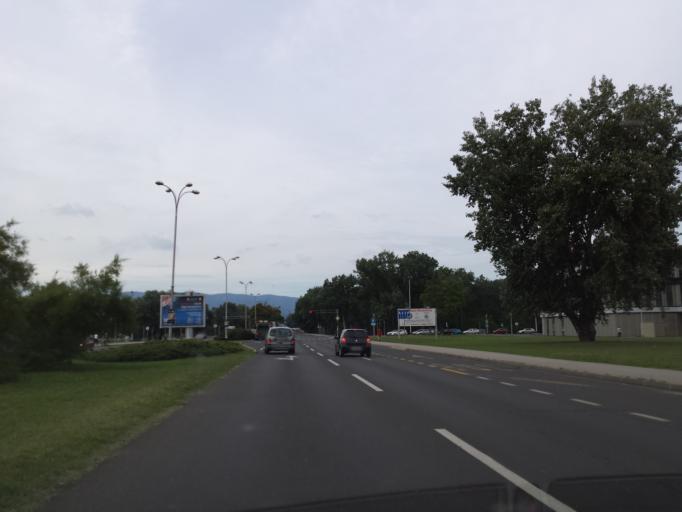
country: HR
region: Grad Zagreb
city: Novi Zagreb
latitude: 45.7823
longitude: 15.9801
